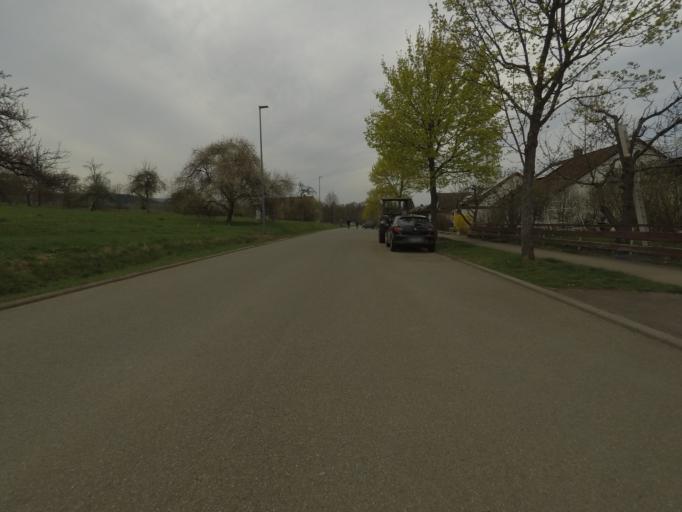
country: DE
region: Baden-Wuerttemberg
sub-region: Tuebingen Region
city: Gomaringen
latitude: 48.4492
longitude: 9.1043
